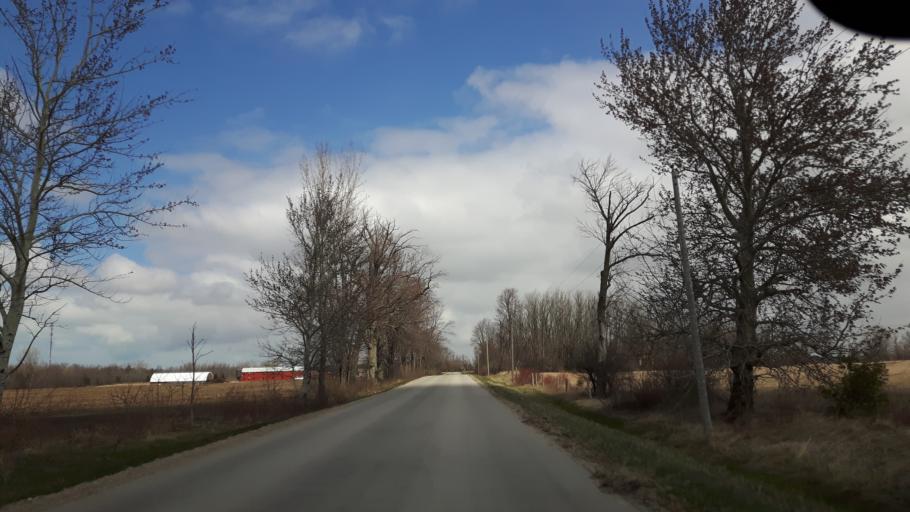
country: CA
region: Ontario
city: Goderich
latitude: 43.7048
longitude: -81.6644
